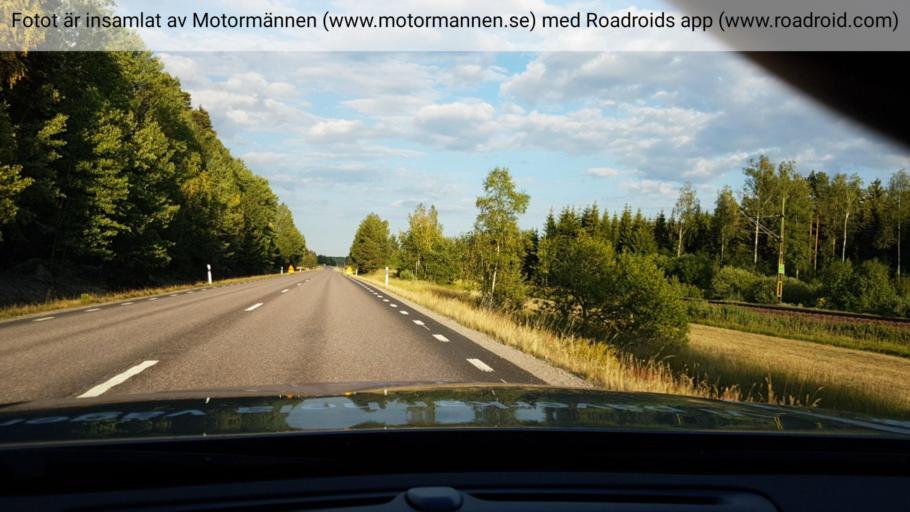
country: SE
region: Uppsala
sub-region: Enkopings Kommun
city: Orsundsbro
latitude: 59.8668
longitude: 17.3294
